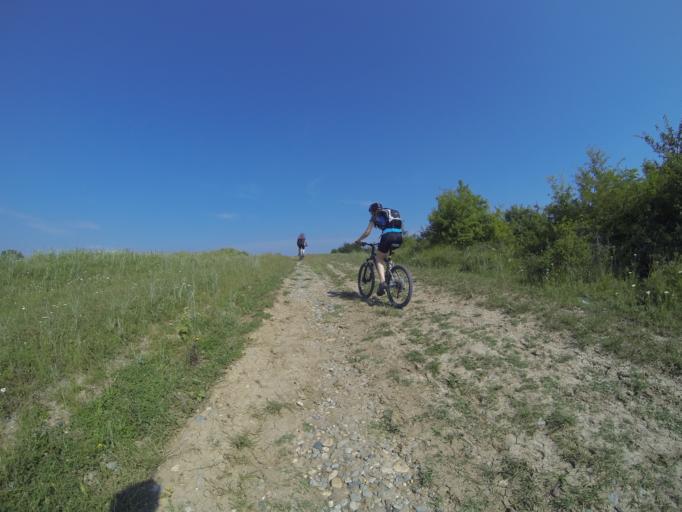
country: RO
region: Gorj
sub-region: Comuna Crusetu
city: Crusetu
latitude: 44.6062
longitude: 23.6799
